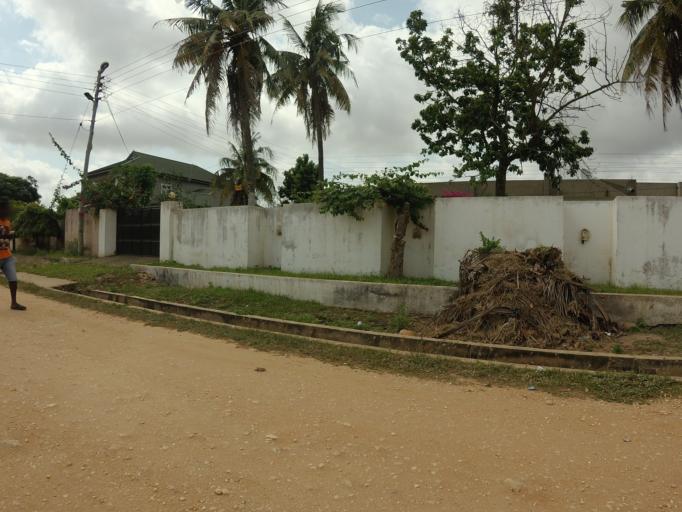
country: GH
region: Greater Accra
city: Dome
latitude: 5.6196
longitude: -0.2438
